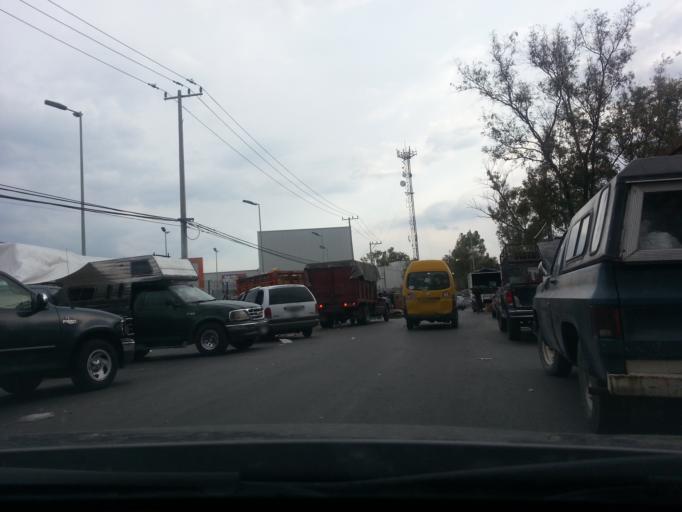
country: MX
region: Mexico
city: Cuautitlan Izcalli
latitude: 19.6212
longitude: -99.2363
